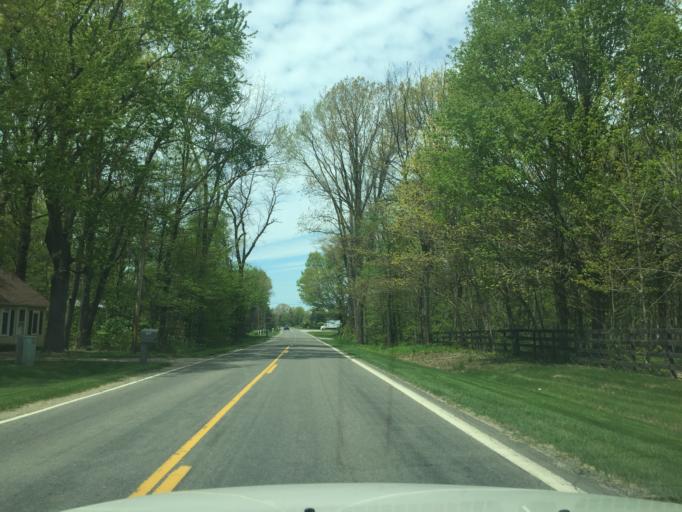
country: US
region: Michigan
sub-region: Berrien County
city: Stevensville
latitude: 41.9902
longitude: -86.5039
